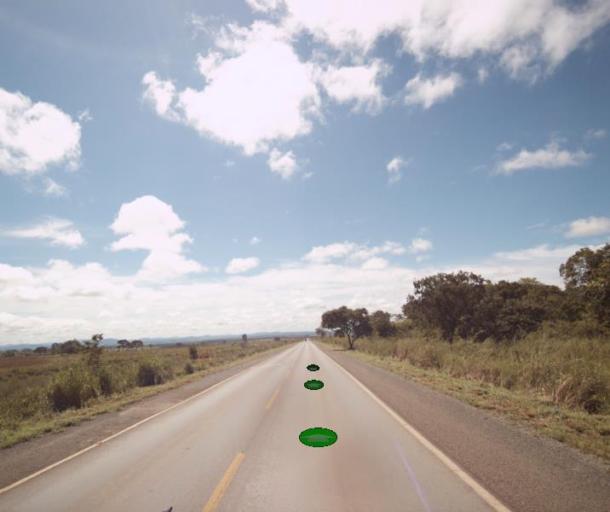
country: BR
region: Goias
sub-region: Padre Bernardo
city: Padre Bernardo
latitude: -15.1754
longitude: -48.4031
